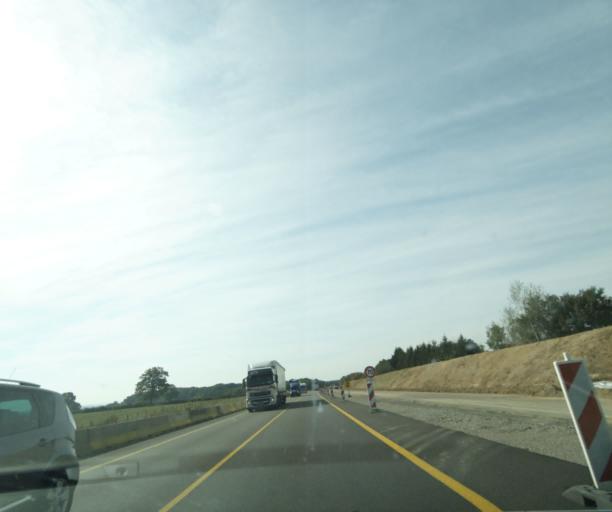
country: FR
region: Bourgogne
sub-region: Departement de Saone-et-Loire
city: Paray-le-Monial
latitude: 46.4984
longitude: 4.1589
